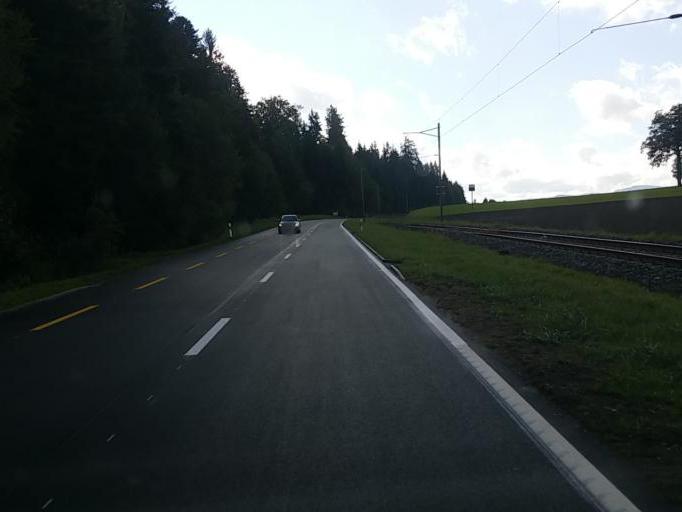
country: CH
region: Bern
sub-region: Emmental District
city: Sumiswald
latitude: 47.0572
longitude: 7.7503
